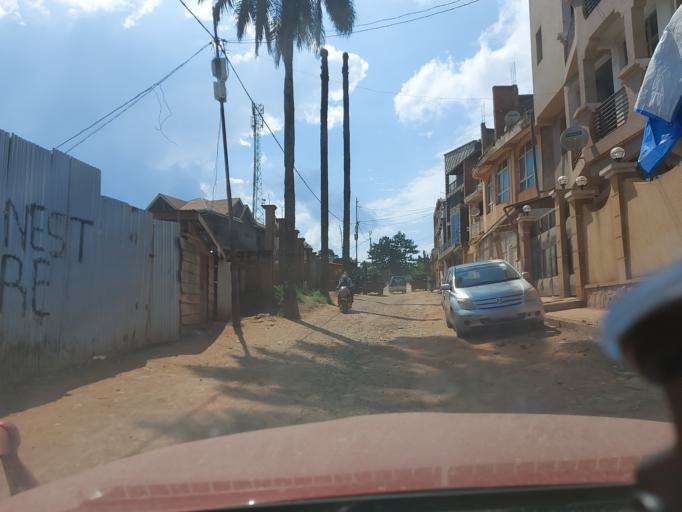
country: CD
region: South Kivu
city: Bukavu
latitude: -2.4984
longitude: 28.8672
